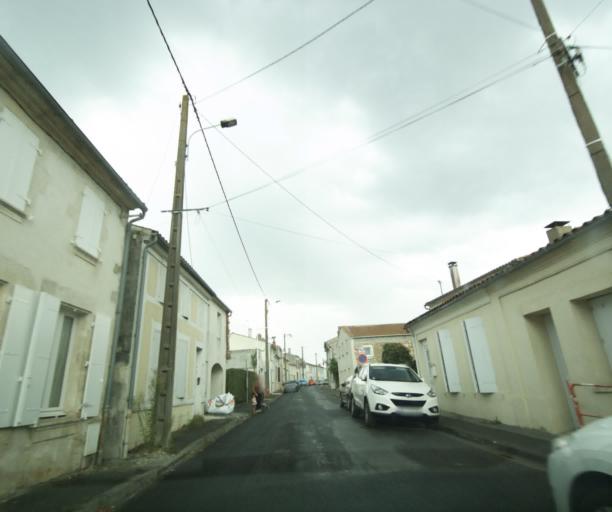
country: FR
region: Poitou-Charentes
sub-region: Departement de la Charente-Maritime
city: Tonnay-Charente
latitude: 45.9477
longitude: -0.8805
